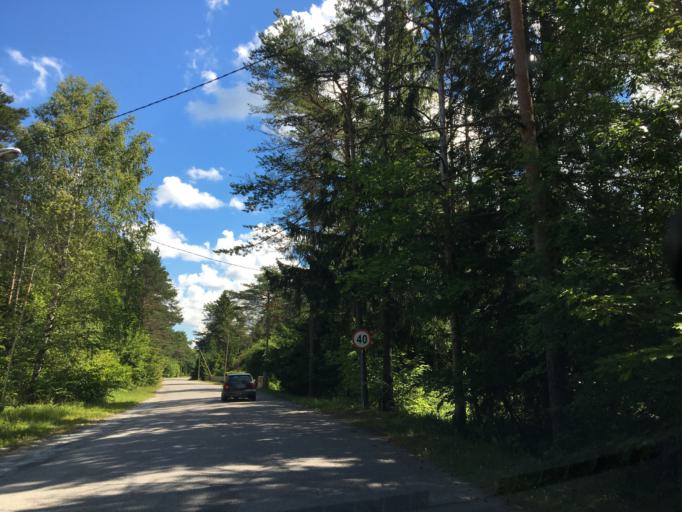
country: EE
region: Harju
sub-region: Nissi vald
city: Riisipere
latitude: 59.2430
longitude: 24.2927
